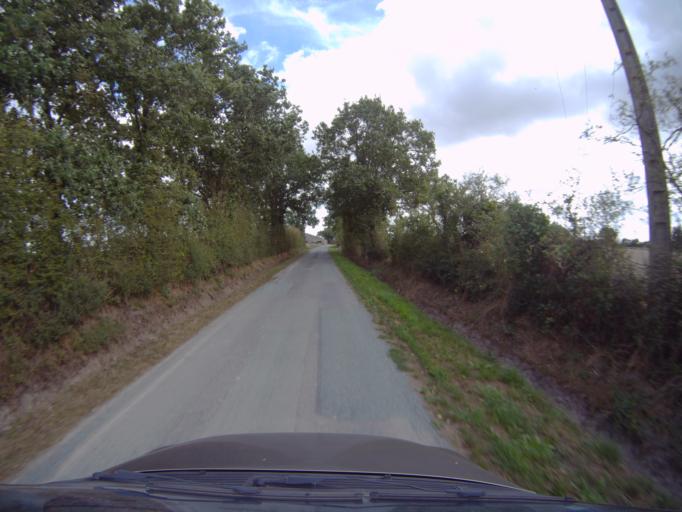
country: FR
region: Pays de la Loire
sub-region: Departement de la Loire-Atlantique
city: La Planche
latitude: 47.0277
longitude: -1.4122
